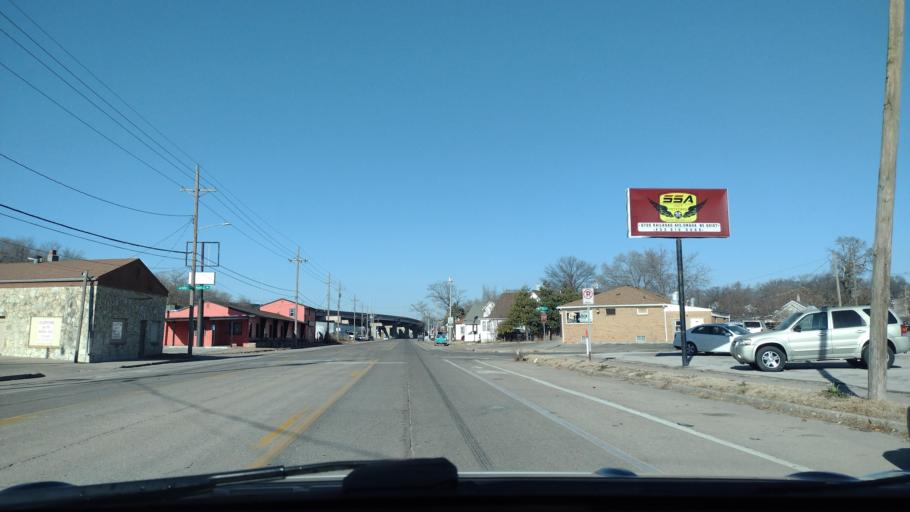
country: US
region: Nebraska
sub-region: Douglas County
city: Omaha
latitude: 41.1925
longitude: -95.9383
